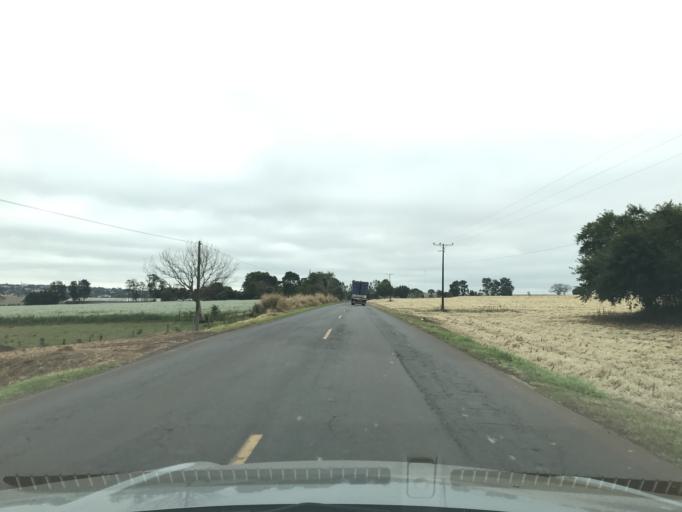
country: BR
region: Parana
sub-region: Ipora
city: Ipora
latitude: -24.0940
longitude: -53.8361
